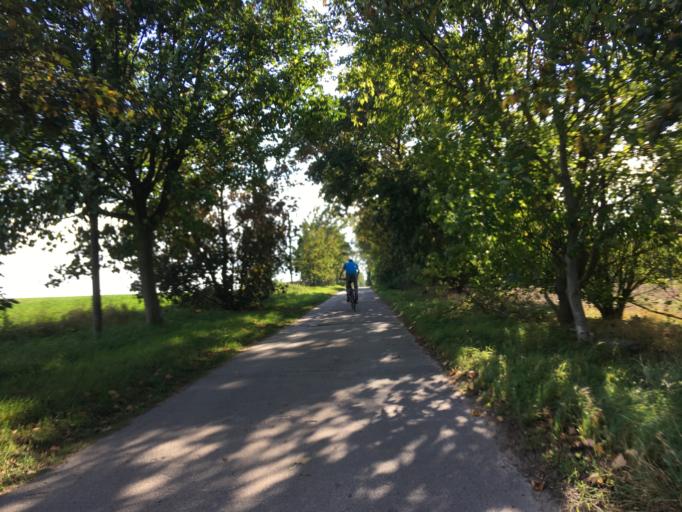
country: DE
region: Brandenburg
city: Altlandsberg
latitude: 52.5539
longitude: 13.7273
